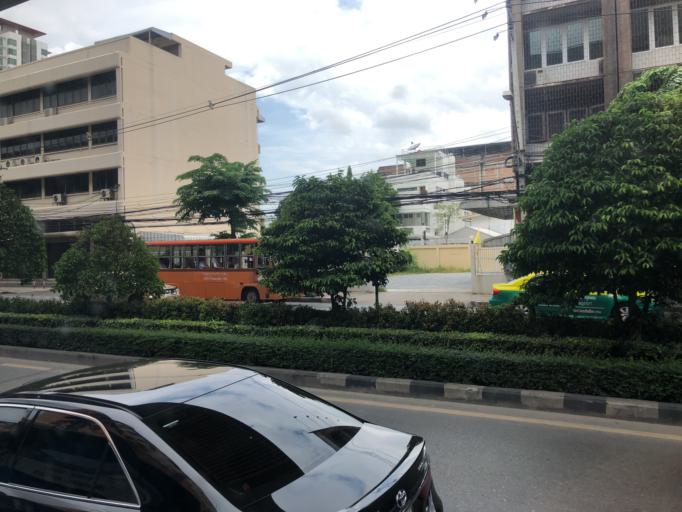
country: TH
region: Bangkok
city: Phra Khanong
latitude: 13.6920
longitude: 100.6078
